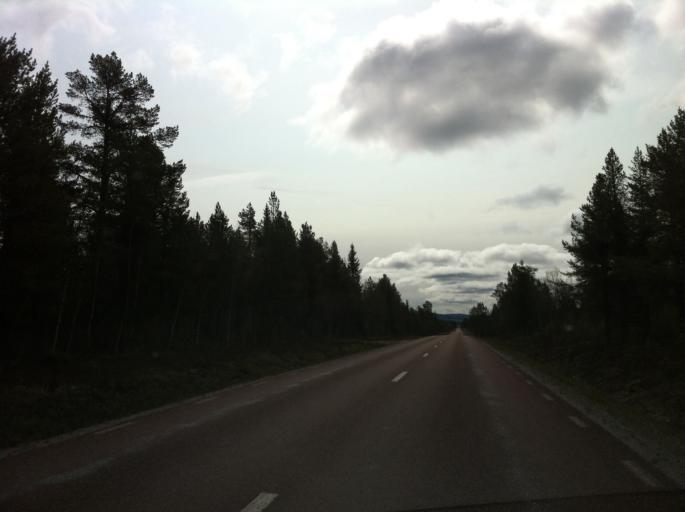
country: NO
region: Hedmark
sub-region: Engerdal
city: Engerdal
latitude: 62.4879
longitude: 12.6487
